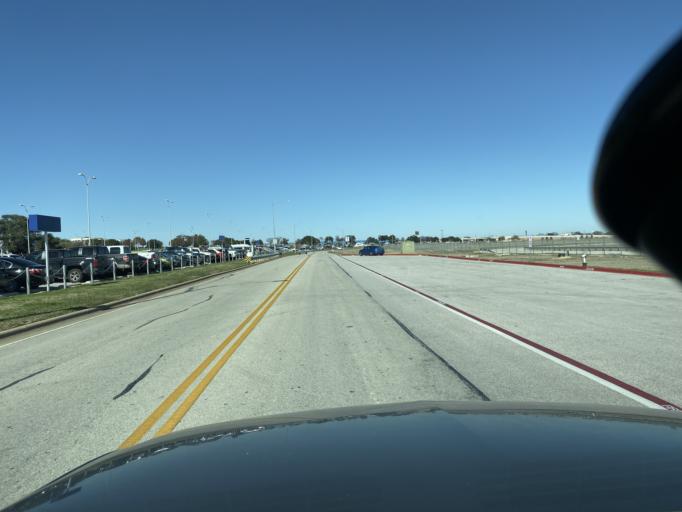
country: US
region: Texas
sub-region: Travis County
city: Hornsby Bend
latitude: 30.2059
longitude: -97.6610
